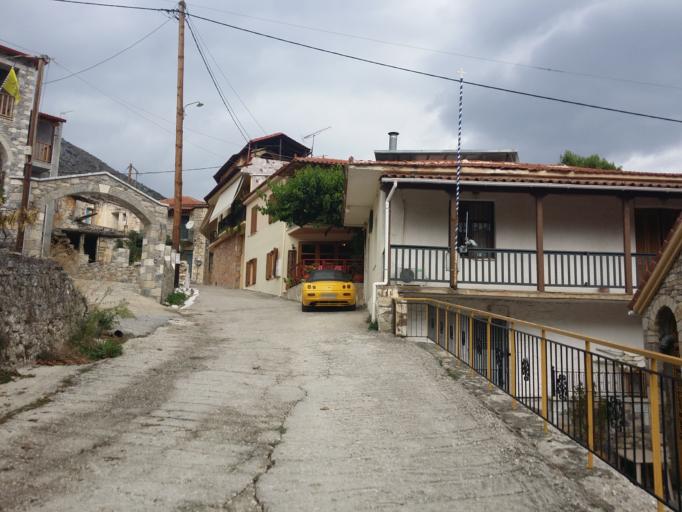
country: GR
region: Peloponnese
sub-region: Nomos Argolidos
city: Koutsopodi
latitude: 37.6394
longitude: 22.5459
